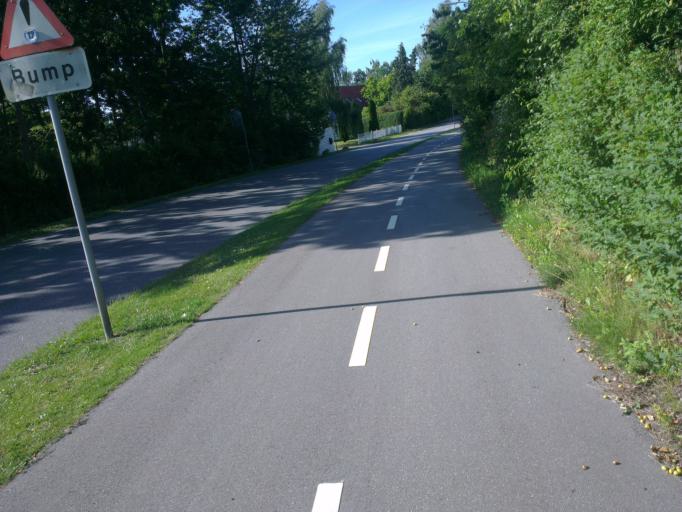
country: DK
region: Capital Region
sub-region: Frederikssund Kommune
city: Skibby
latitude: 55.7469
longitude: 11.9641
